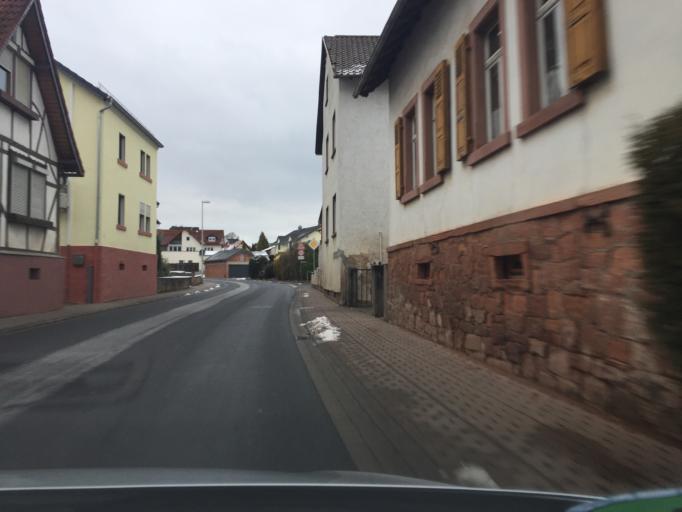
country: DE
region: Bavaria
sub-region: Regierungsbezirk Unterfranken
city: Schollkrippen
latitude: 50.0952
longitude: 9.2384
